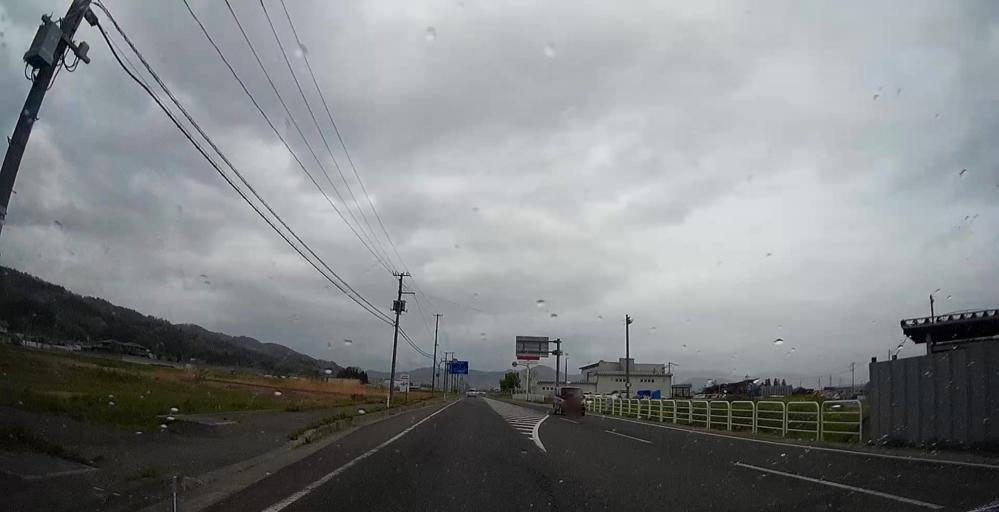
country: JP
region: Yamagata
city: Nagai
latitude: 38.0566
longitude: 140.1036
